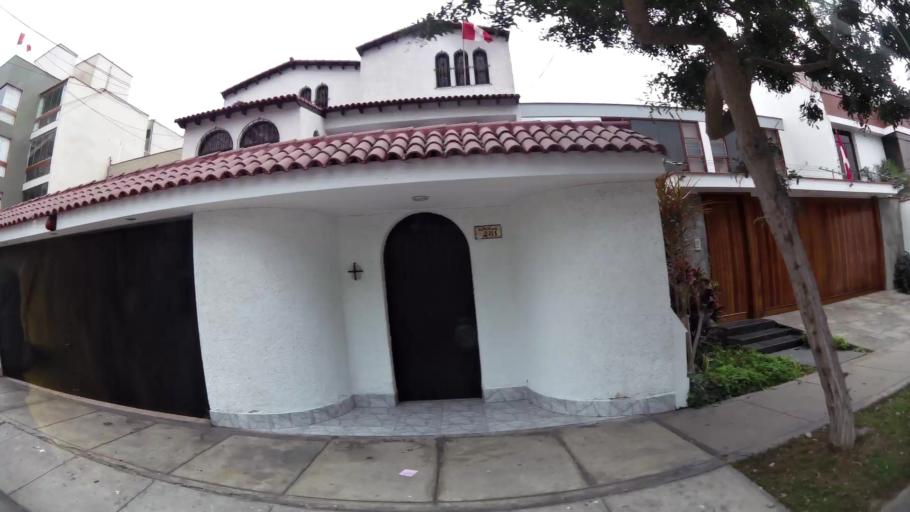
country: PE
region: Lima
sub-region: Lima
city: Surco
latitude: -12.1307
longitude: -77.0156
